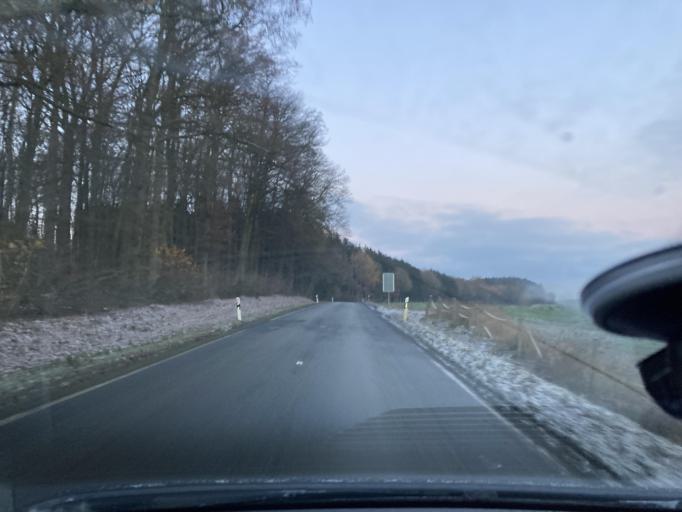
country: DE
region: Rheinland-Pfalz
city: Wurrich
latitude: 49.9723
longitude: 7.2967
